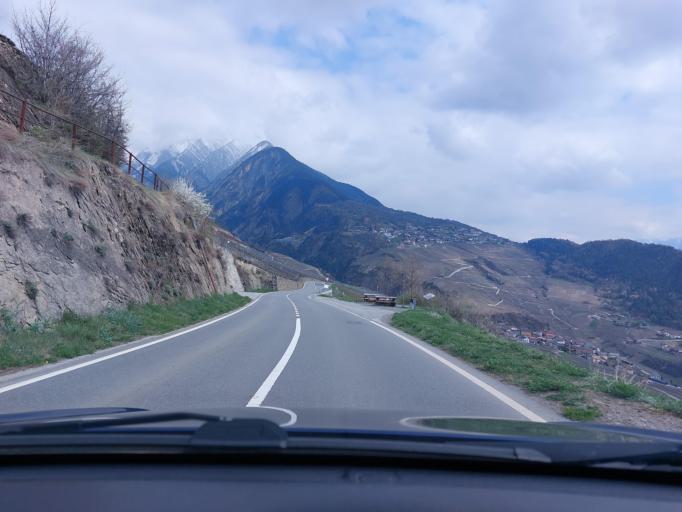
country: CH
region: Valais
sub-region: Conthey District
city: Conthey
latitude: 46.2379
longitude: 7.2963
